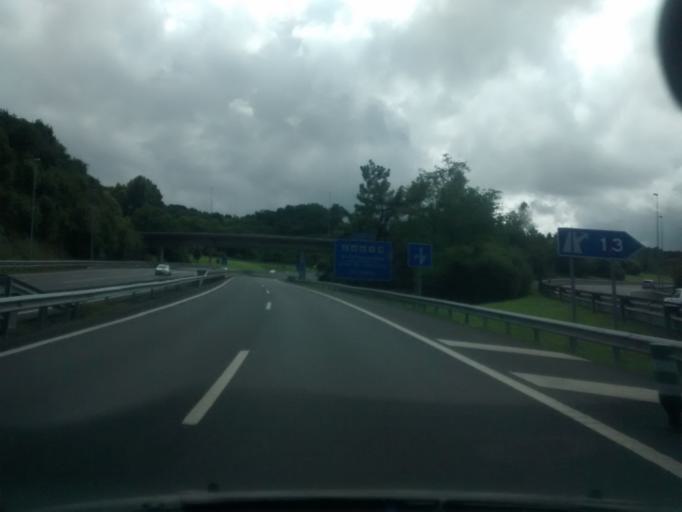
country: ES
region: Basque Country
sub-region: Provincia de Guipuzcoa
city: Lasarte
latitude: 43.2926
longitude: -2.0171
